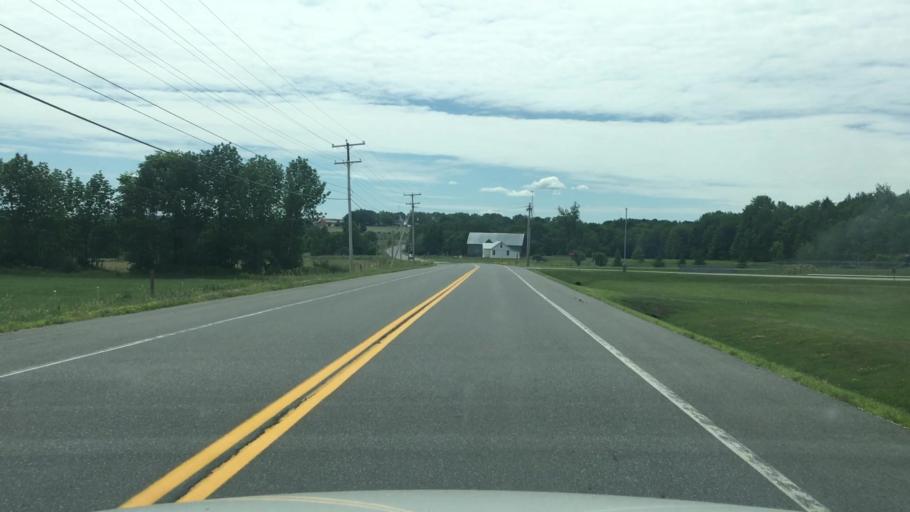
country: US
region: Maine
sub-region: Waldo County
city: Troy
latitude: 44.5517
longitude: -69.2684
